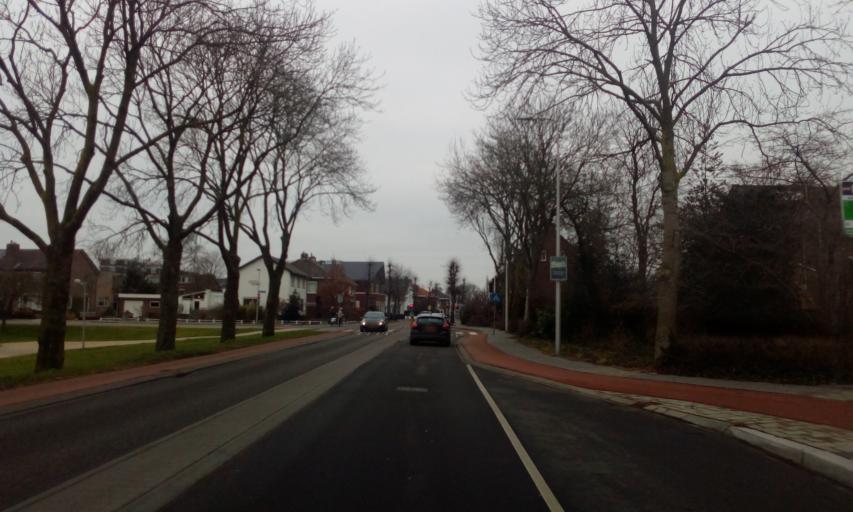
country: NL
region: South Holland
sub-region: Gemeente Waddinxveen
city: Waddinxveen
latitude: 52.0426
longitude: 4.6536
